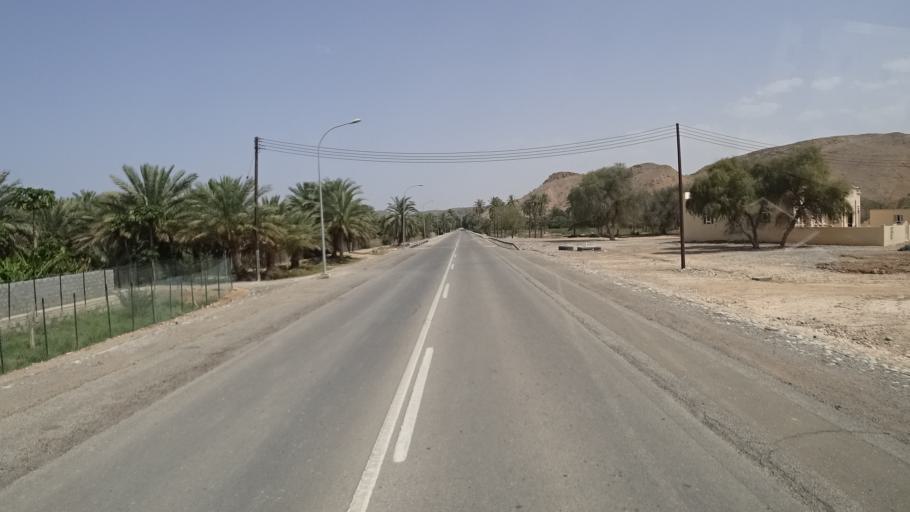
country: OM
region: Muhafazat Masqat
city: Muscat
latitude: 23.1723
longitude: 58.9140
